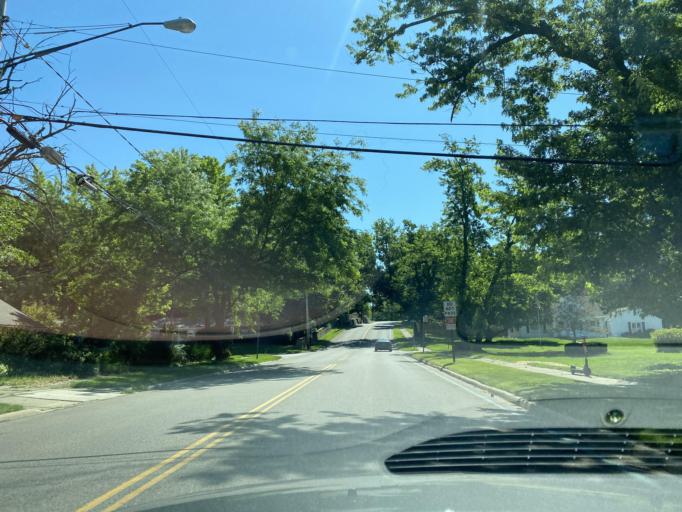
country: US
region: Ohio
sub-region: Summit County
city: Akron
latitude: 41.1164
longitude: -81.5540
